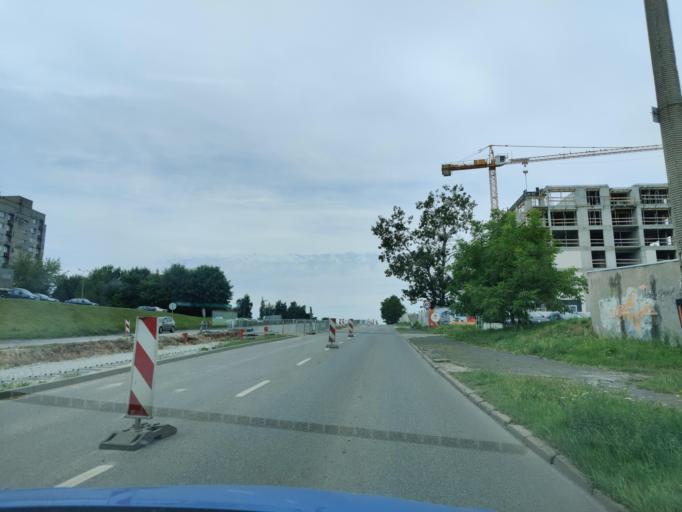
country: PL
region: Silesian Voivodeship
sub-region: Dabrowa Gornicza
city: Dabrowa Gornicza
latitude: 50.2827
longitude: 19.1896
